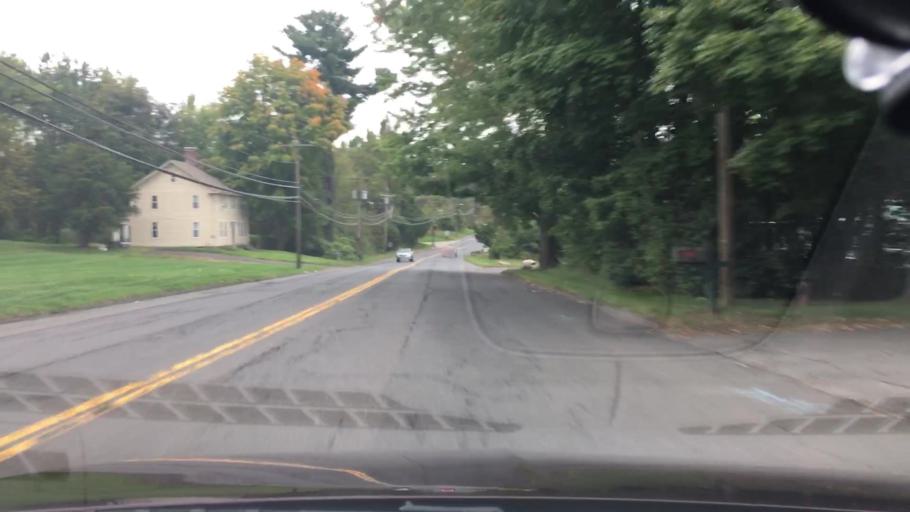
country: US
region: Connecticut
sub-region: Middlesex County
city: Middletown
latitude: 41.5771
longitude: -72.7229
